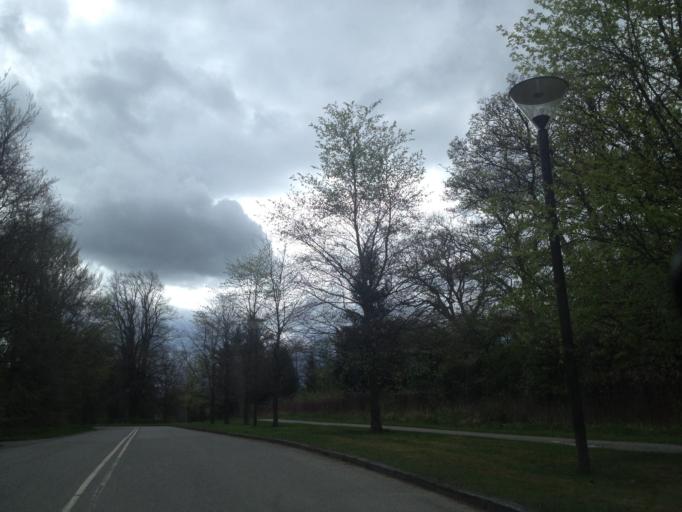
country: DK
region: Capital Region
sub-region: Horsholm Kommune
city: Horsholm
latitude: 55.8725
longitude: 12.4890
